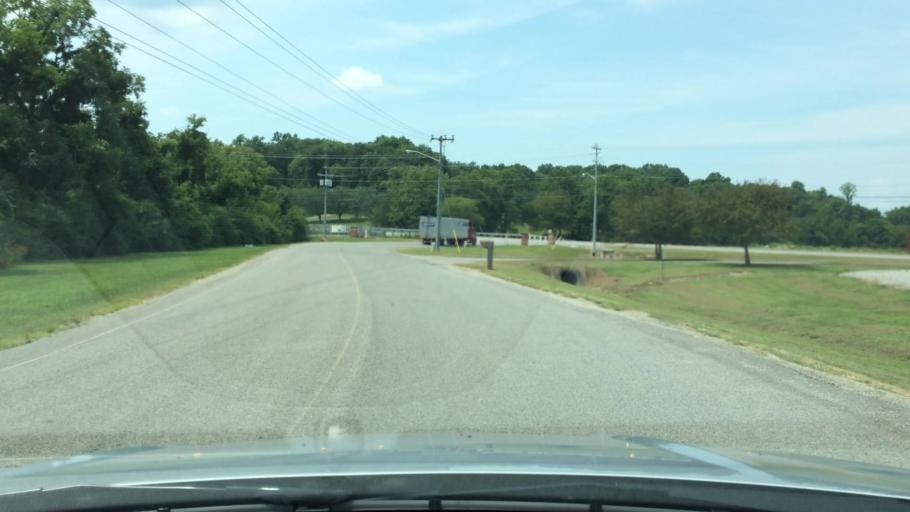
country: US
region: Tennessee
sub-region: Giles County
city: Pulaski
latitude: 35.1510
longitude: -87.0009
